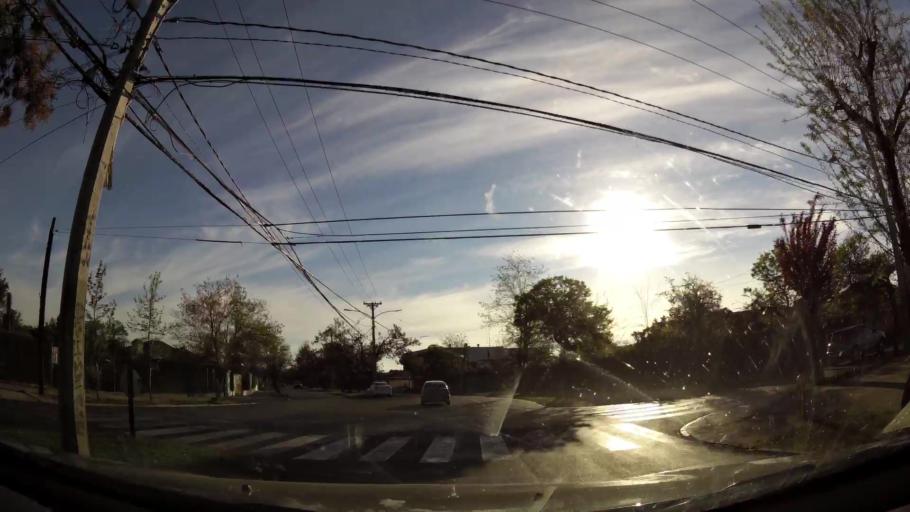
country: CL
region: Santiago Metropolitan
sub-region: Provincia de Cordillera
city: Puente Alto
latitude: -33.6064
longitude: -70.5807
